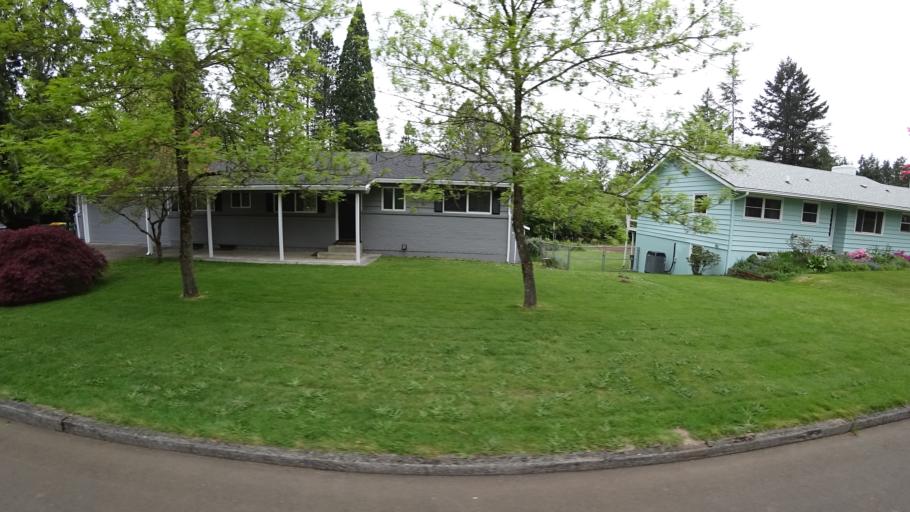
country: US
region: Oregon
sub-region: Washington County
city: Beaverton
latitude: 45.4628
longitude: -122.8251
